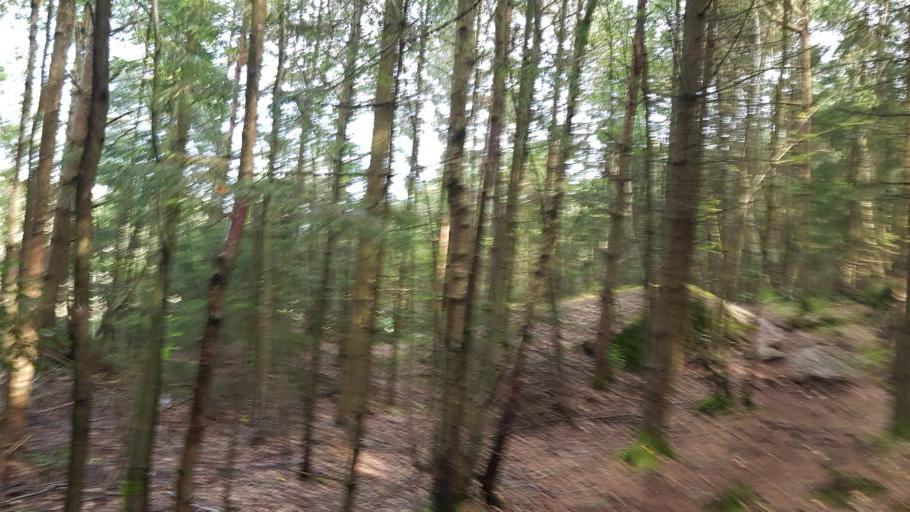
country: SE
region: Vaestra Goetaland
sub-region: Molndal
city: Moelndal
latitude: 57.6729
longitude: 12.0304
